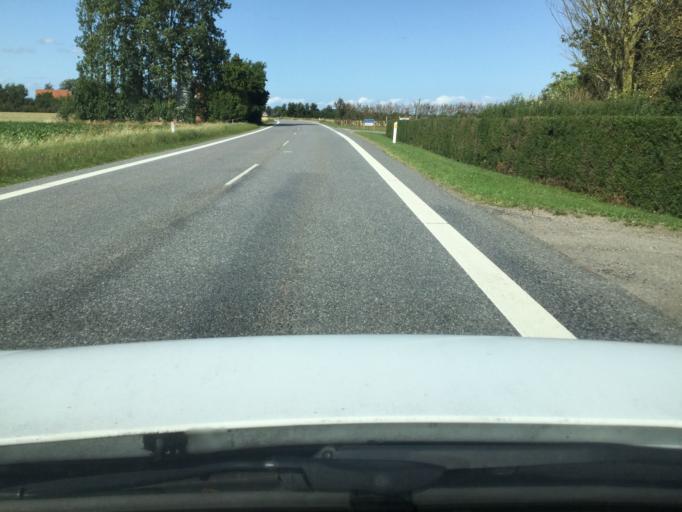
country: DK
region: Zealand
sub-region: Lolland Kommune
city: Rodby
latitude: 54.7349
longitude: 11.3895
